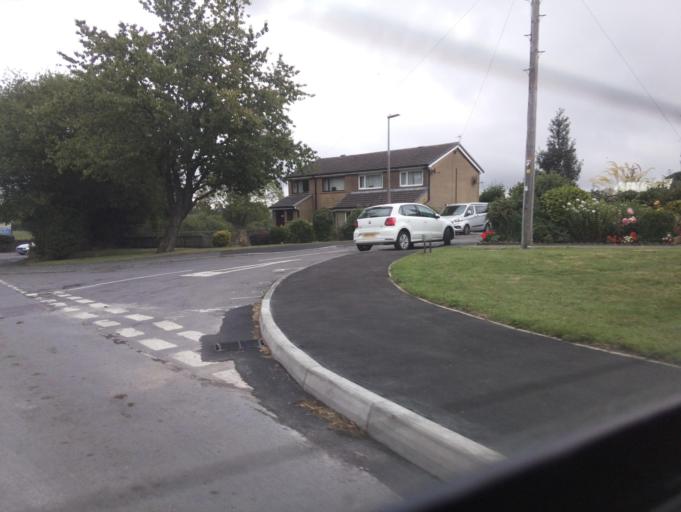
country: GB
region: England
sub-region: Kirklees
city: Shelley
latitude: 53.5978
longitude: -1.6845
